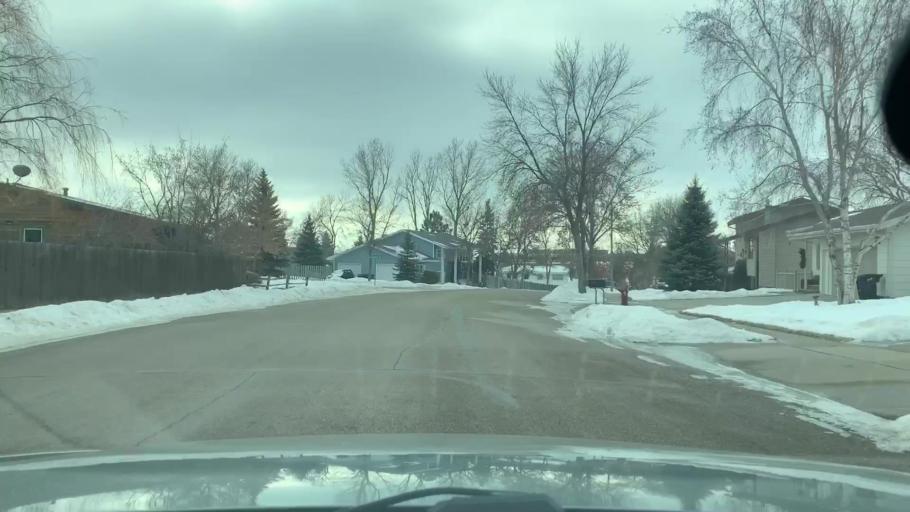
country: US
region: North Dakota
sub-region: Burleigh County
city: Bismarck
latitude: 46.8260
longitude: -100.8067
